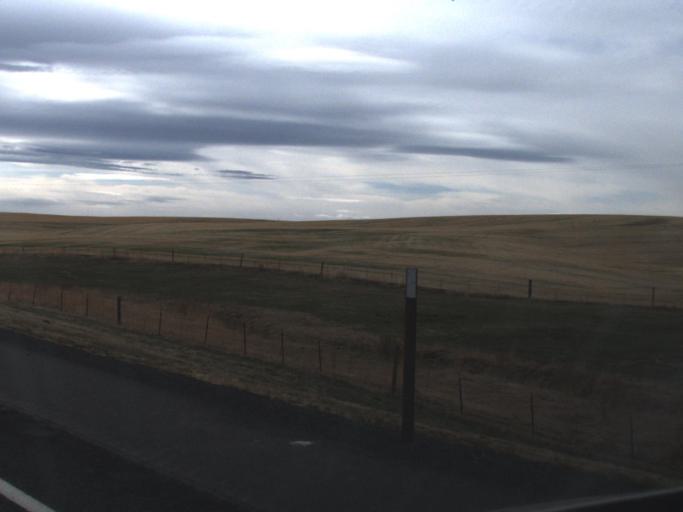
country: US
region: Washington
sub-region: Asotin County
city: Clarkston
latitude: 46.4984
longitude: -117.0778
